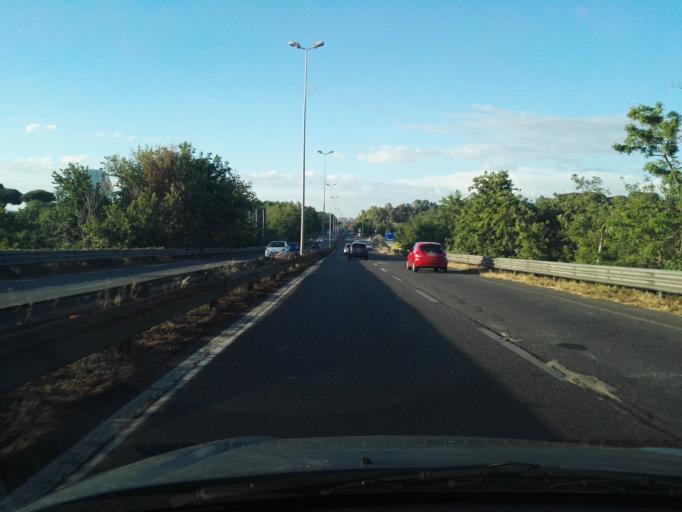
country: IT
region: Latium
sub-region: Citta metropolitana di Roma Capitale
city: Selcetta
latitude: 41.8073
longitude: 12.4566
